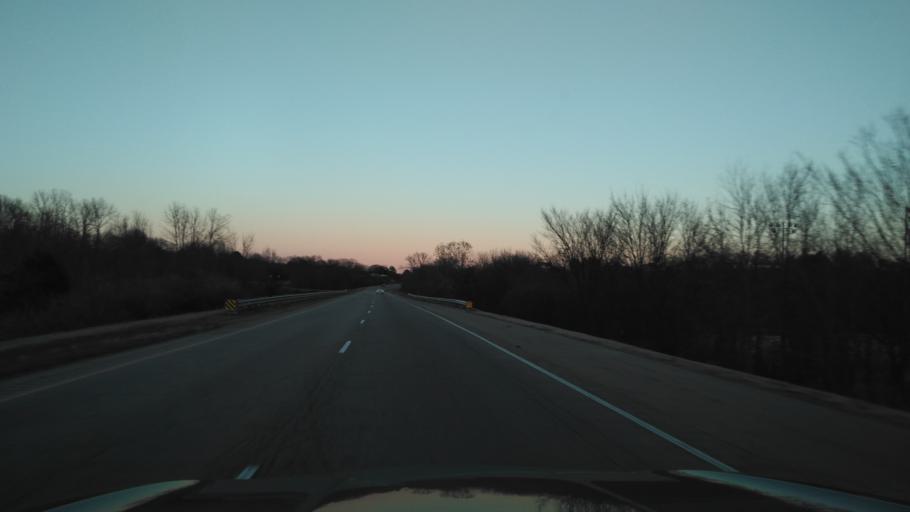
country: US
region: Arkansas
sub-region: Crawford County
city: Van Buren
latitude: 35.4618
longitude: -94.3867
